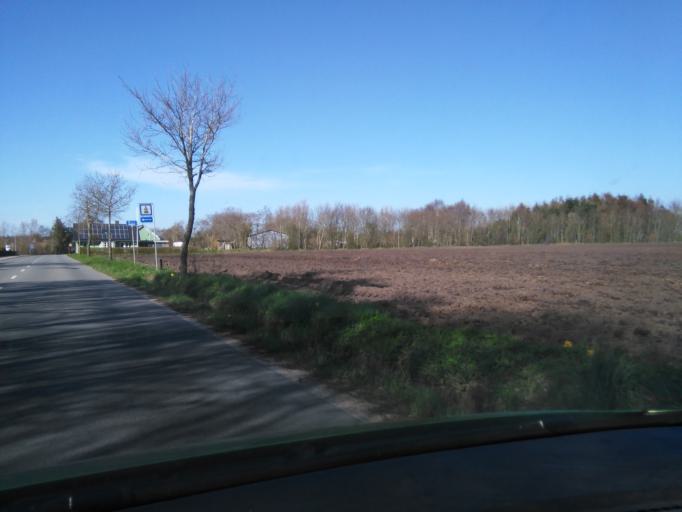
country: DK
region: South Denmark
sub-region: Varde Kommune
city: Oksbol
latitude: 55.6403
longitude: 8.2822
